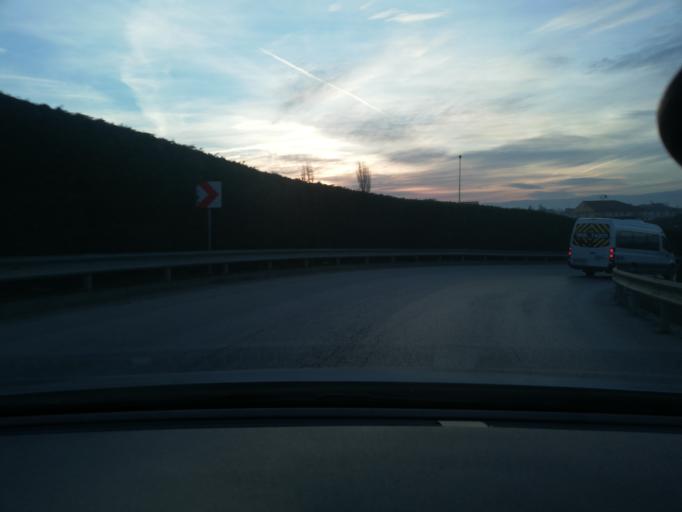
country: TR
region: Duzce
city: Duzce
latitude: 40.8378
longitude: 31.1748
